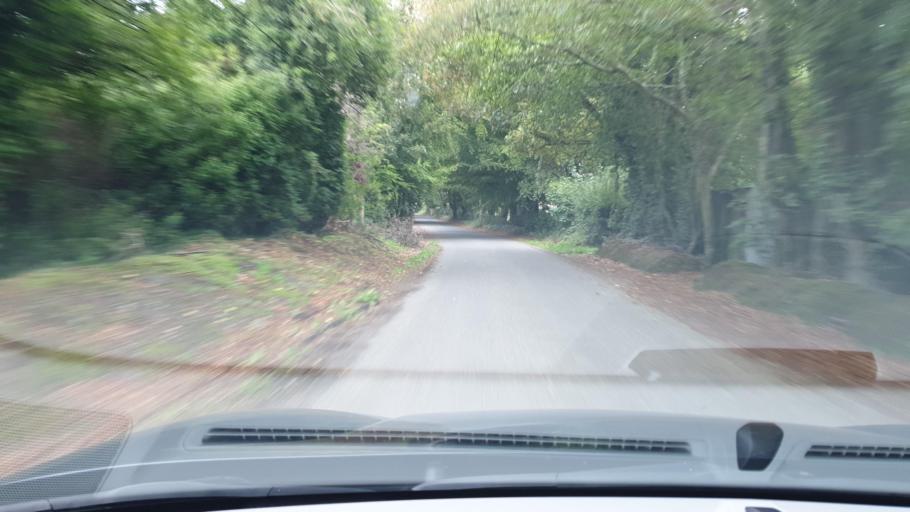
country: IE
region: Leinster
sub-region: An Mhi
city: Dunshaughlin
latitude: 53.5598
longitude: -6.5141
